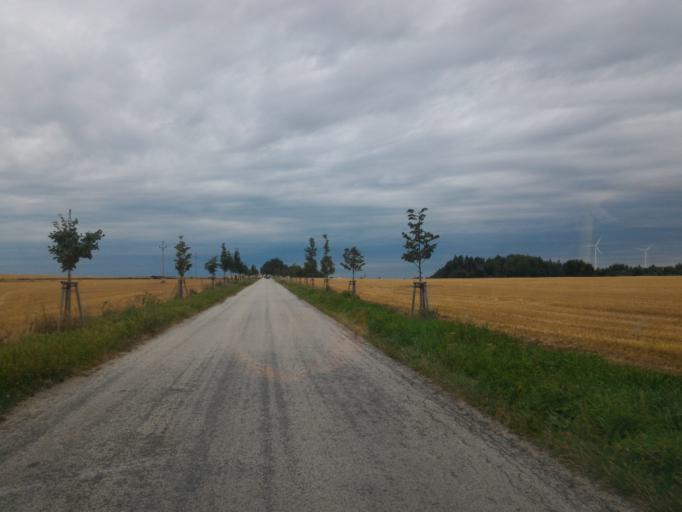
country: CZ
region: Vysocina
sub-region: Okres Jihlava
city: Trest'
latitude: 49.2408
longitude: 15.5726
